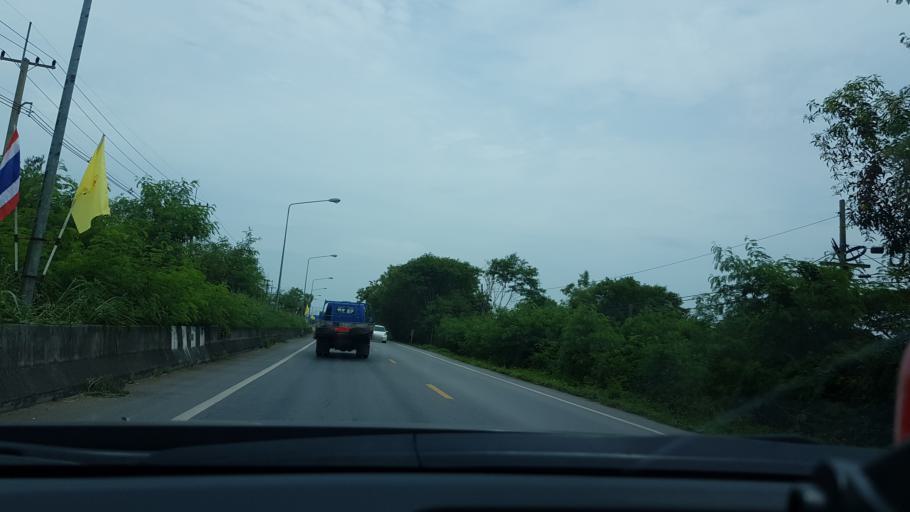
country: TH
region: Pathum Thani
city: Sam Khok
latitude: 14.1276
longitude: 100.5420
